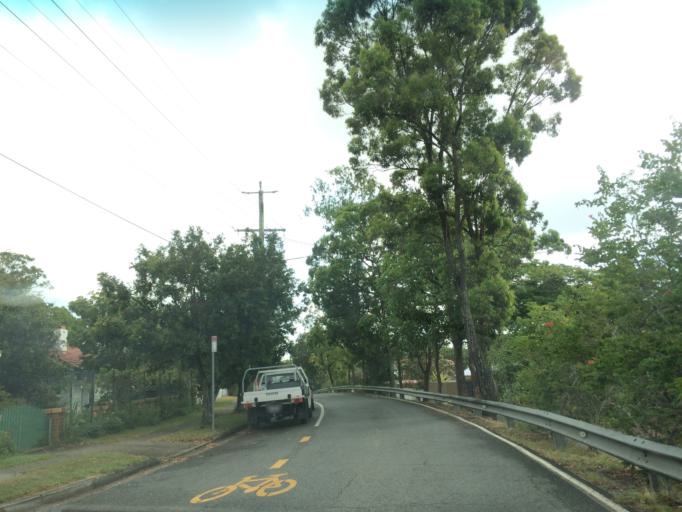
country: AU
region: Queensland
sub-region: Brisbane
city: Yeronga
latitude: -27.5037
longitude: 153.0042
